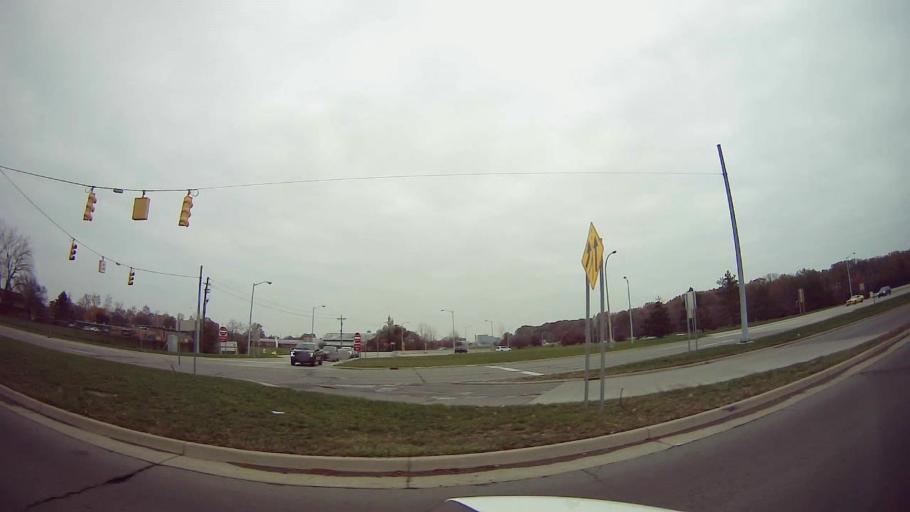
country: US
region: Michigan
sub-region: Wayne County
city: Dearborn Heights
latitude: 42.3297
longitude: -83.2349
